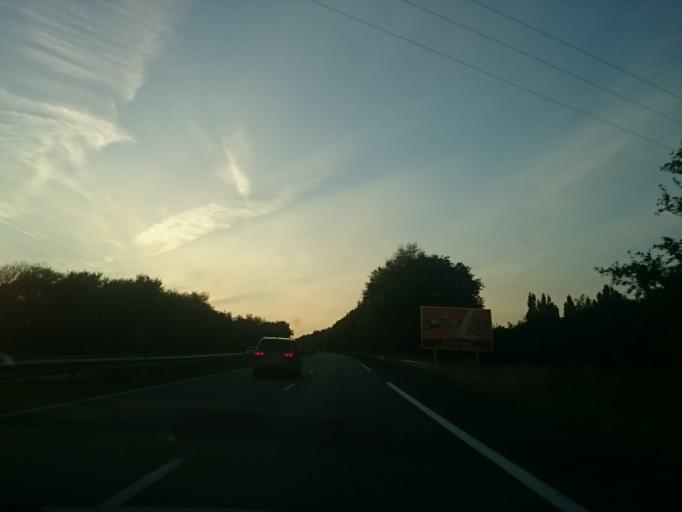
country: FR
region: Brittany
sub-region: Departement du Finistere
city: Melgven
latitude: 47.9154
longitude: -3.8732
